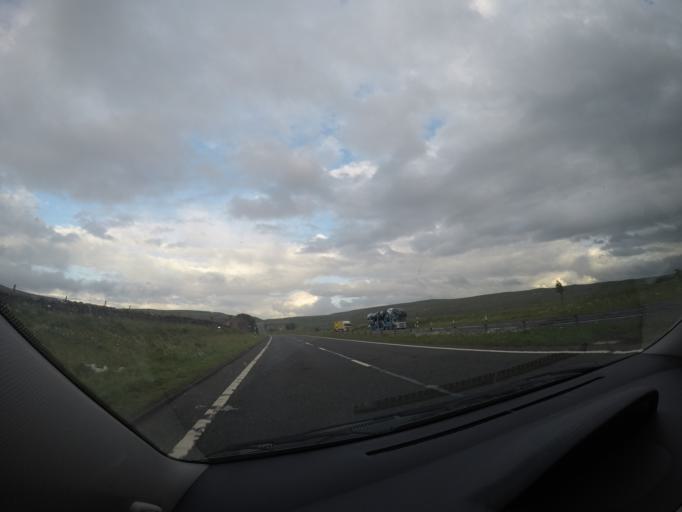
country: GB
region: England
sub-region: County Durham
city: Holwick
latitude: 54.5205
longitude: -2.2193
